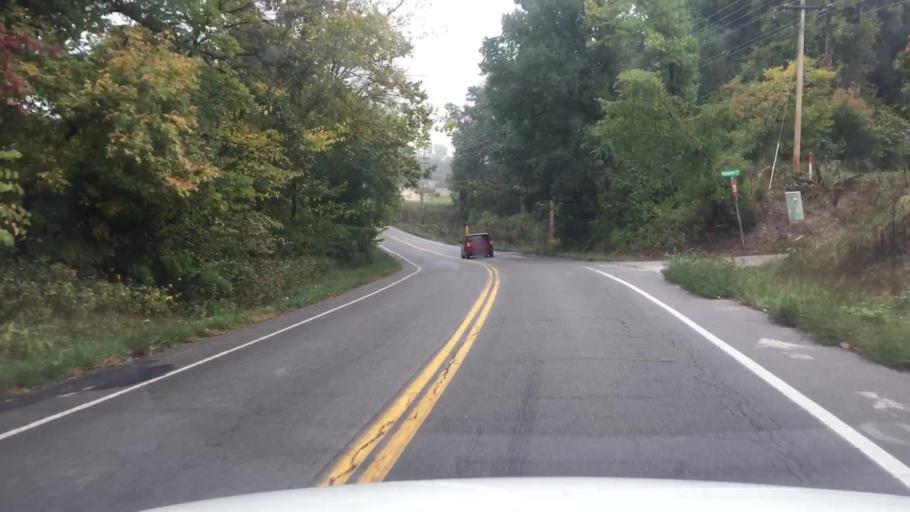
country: US
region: Missouri
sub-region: Boone County
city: Columbia
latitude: 38.8722
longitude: -92.3740
